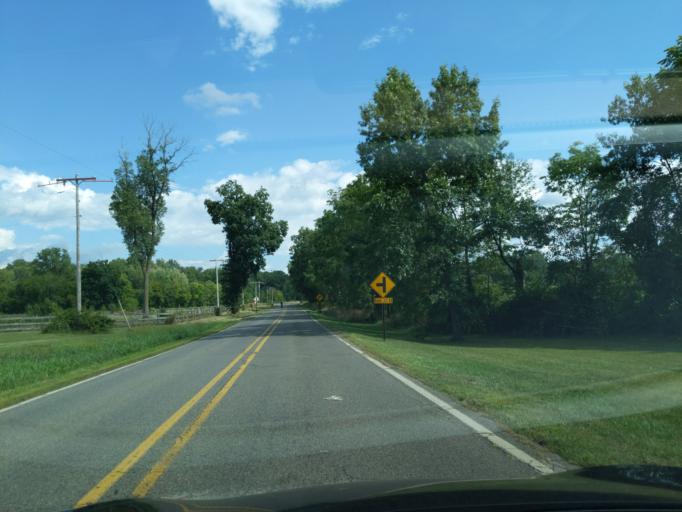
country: US
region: Michigan
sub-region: Jackson County
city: Jackson
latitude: 42.2877
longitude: -84.4653
